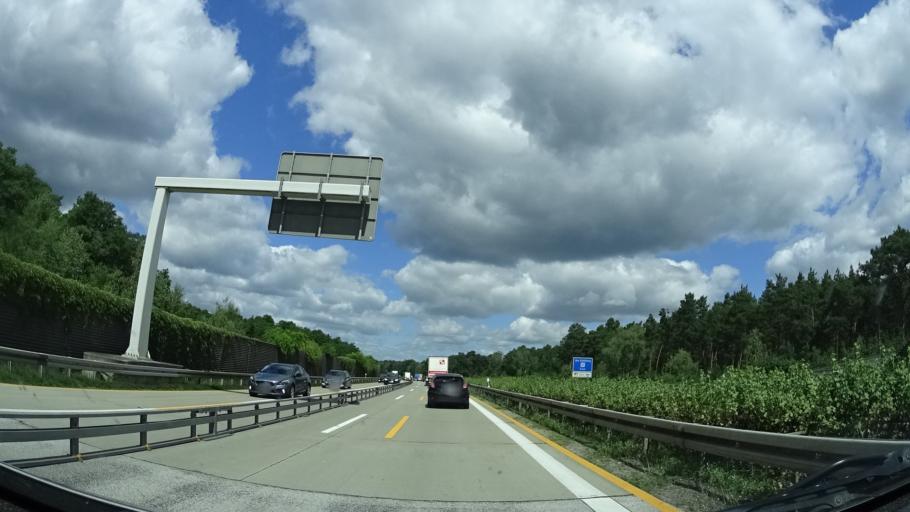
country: DE
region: Brandenburg
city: Schwerin
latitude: 52.1662
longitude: 13.6407
